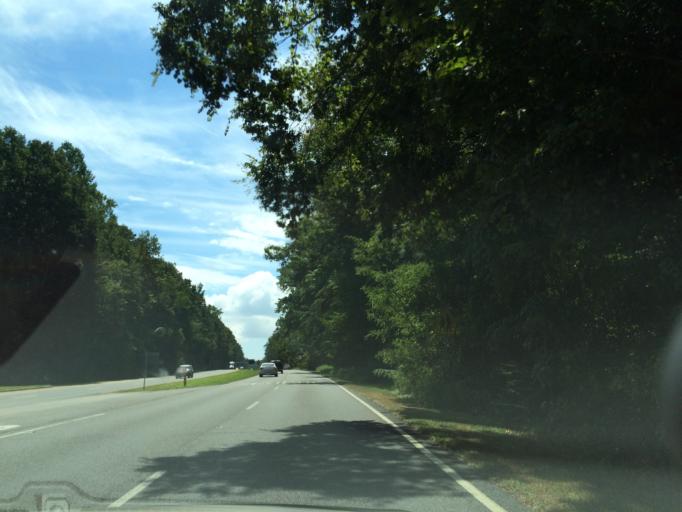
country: US
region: Virginia
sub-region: York County
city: Yorktown
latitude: 37.2280
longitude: -76.5153
